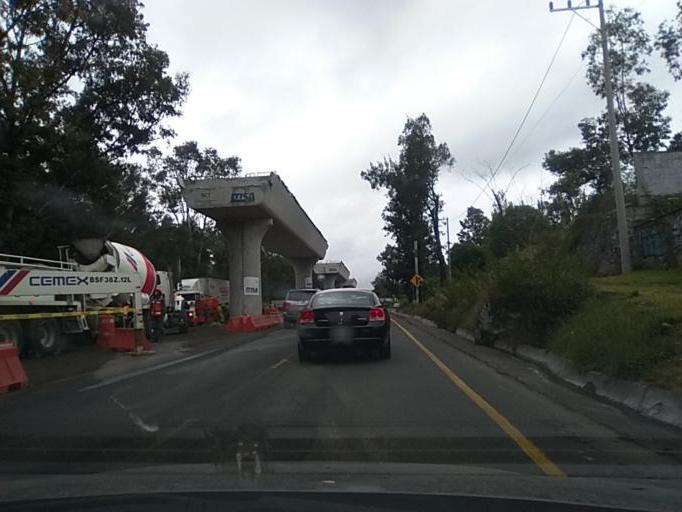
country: MX
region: Mexico City
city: Tlalpan
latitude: 19.2591
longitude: -99.1633
